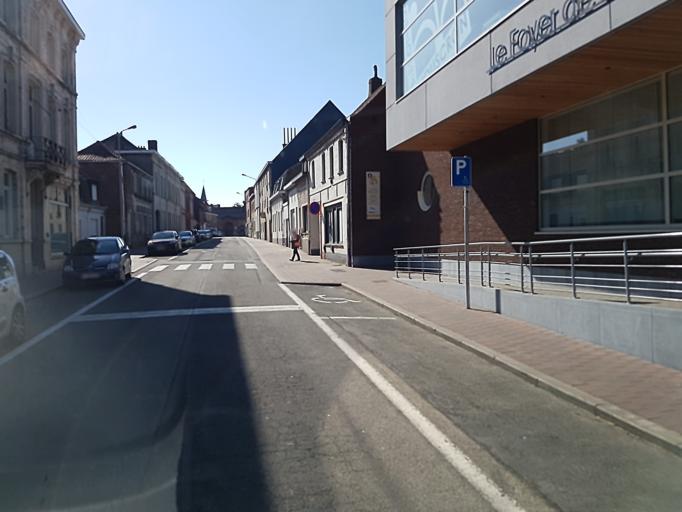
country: BE
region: Wallonia
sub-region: Province du Hainaut
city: Estaimpuis
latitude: 50.7303
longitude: 3.3021
